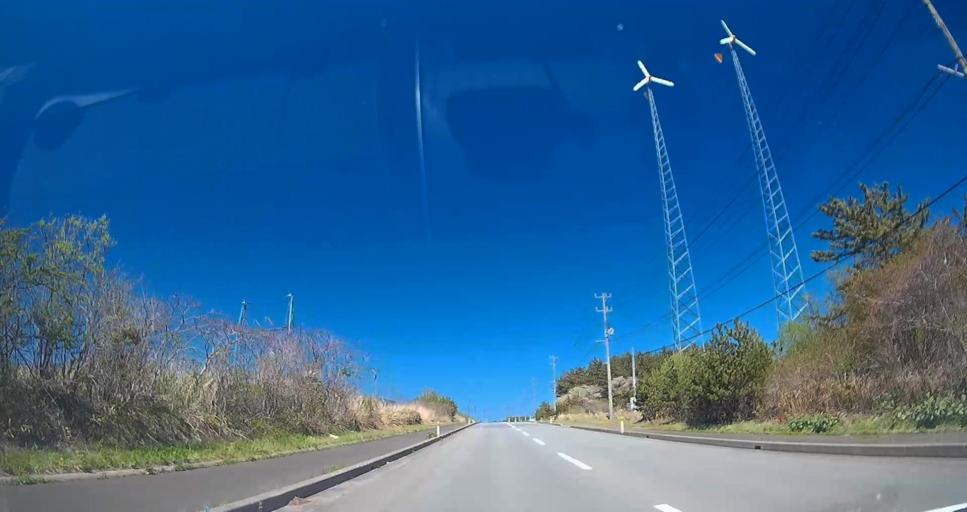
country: JP
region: Hokkaido
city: Hakodate
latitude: 41.5066
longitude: 140.9162
